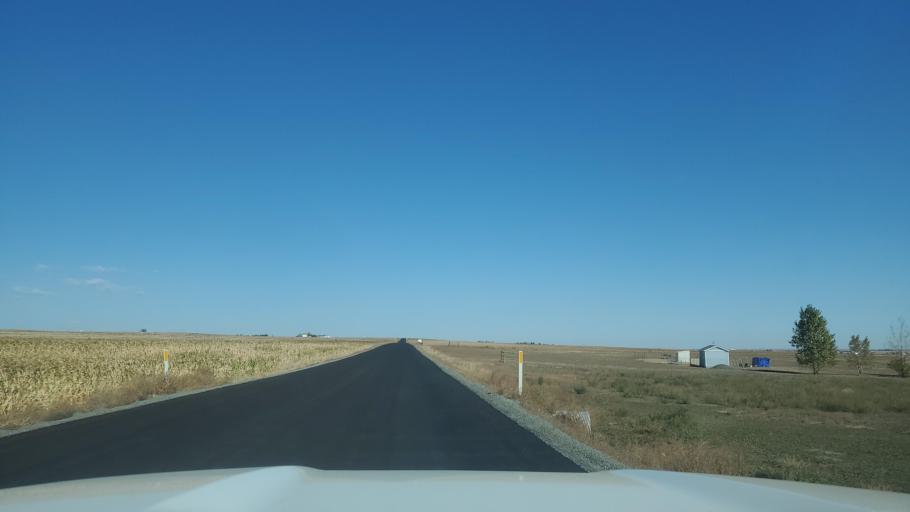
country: US
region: Colorado
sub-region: Adams County
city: Bennett
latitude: 39.7438
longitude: -104.3773
